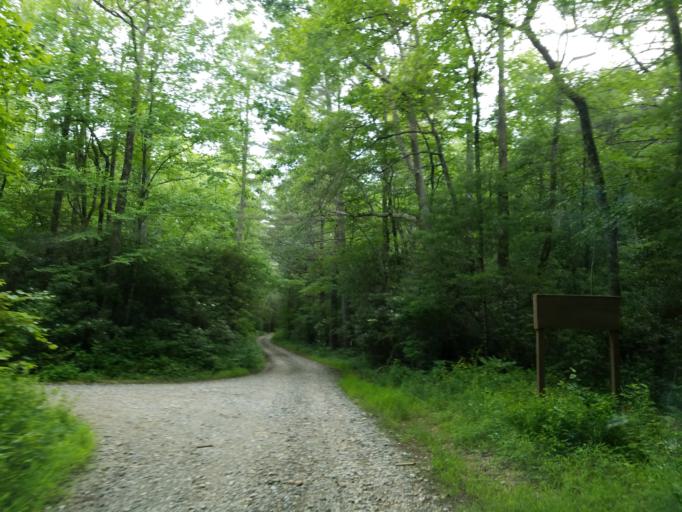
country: US
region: Georgia
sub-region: Union County
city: Blairsville
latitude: 34.7798
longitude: -84.0371
